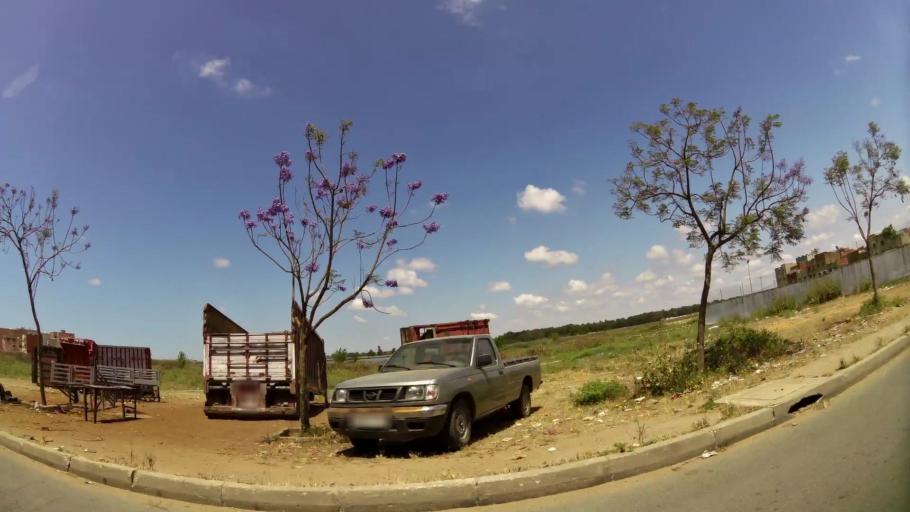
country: MA
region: Gharb-Chrarda-Beni Hssen
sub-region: Kenitra Province
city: Kenitra
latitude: 34.2586
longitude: -6.5497
